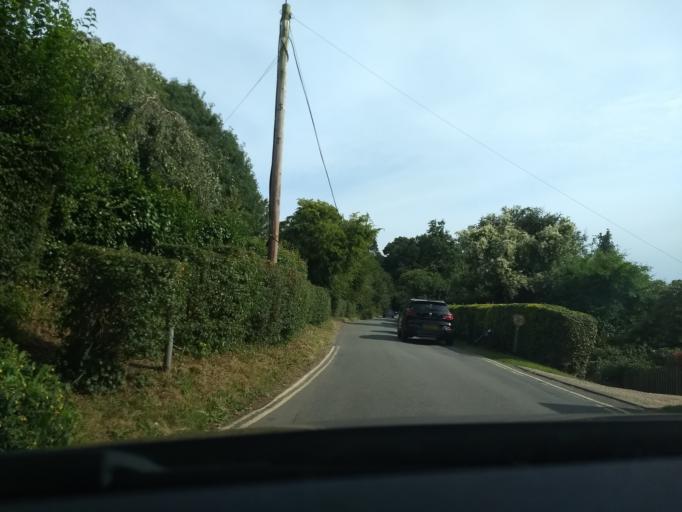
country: GB
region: England
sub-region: Suffolk
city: Shotley Gate
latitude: 51.9937
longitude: 1.2126
